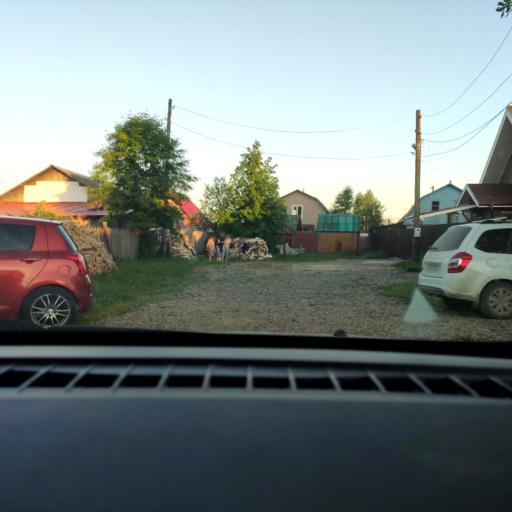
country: RU
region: Perm
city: Polazna
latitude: 58.1745
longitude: 56.4013
